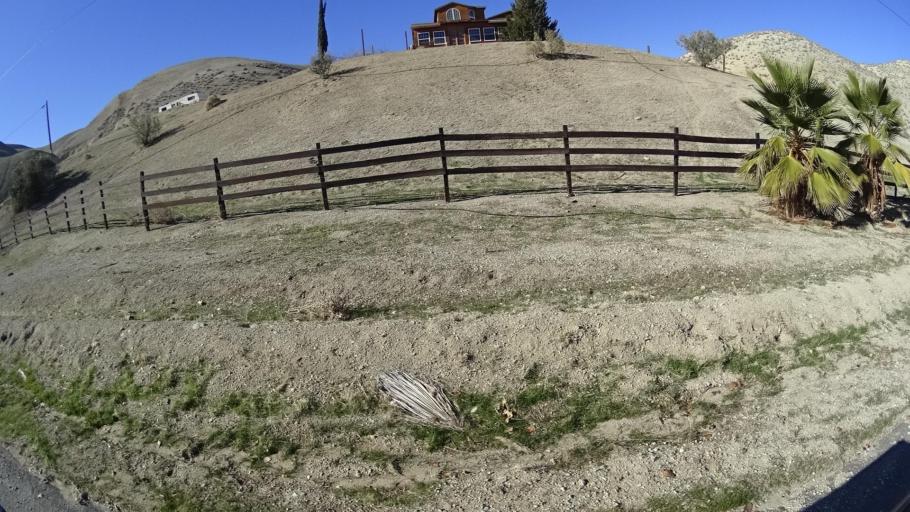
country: US
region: California
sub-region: Kern County
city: Maricopa
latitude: 34.9761
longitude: -119.4084
